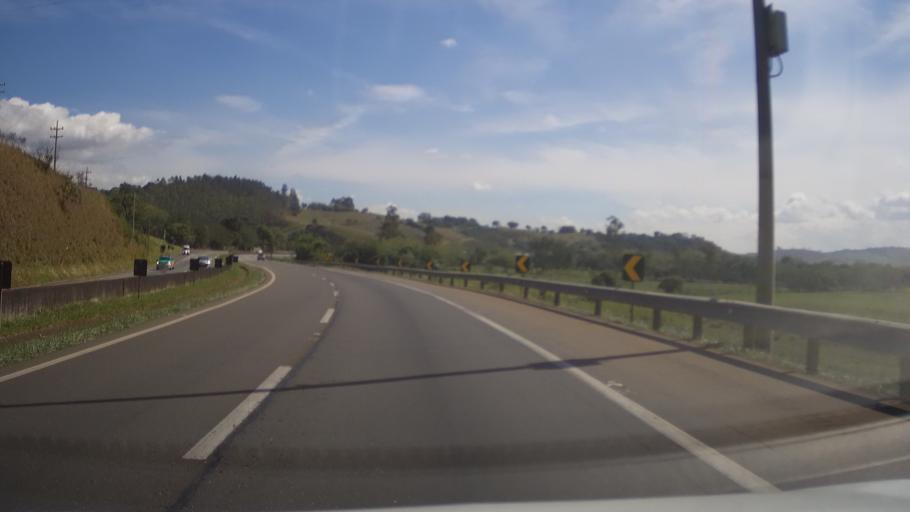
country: BR
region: Minas Gerais
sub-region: Cambui
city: Cambui
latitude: -22.5419
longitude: -46.0376
